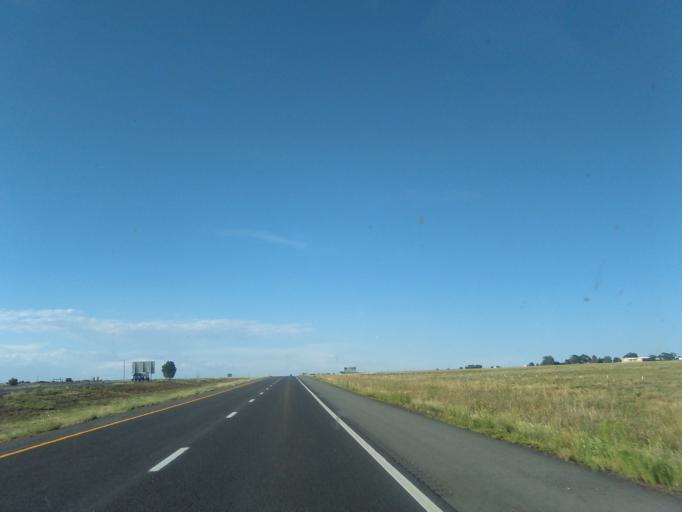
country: US
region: New Mexico
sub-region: San Miguel County
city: Las Vegas
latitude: 35.6471
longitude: -105.1935
